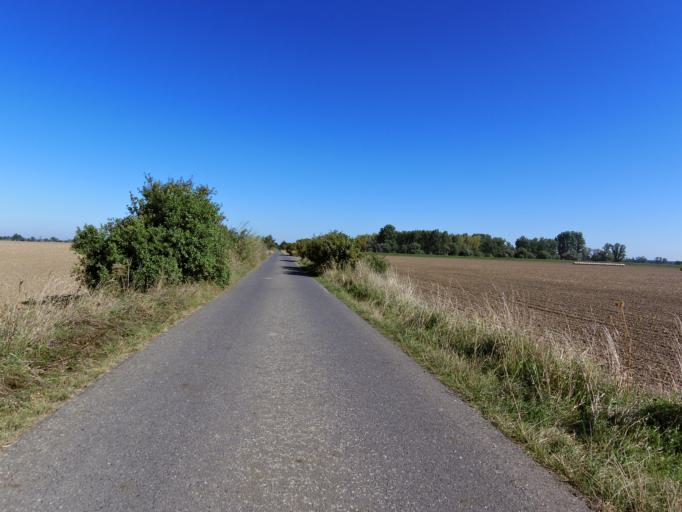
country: DE
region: Saxony
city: Elsnig
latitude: 51.6323
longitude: 12.9141
